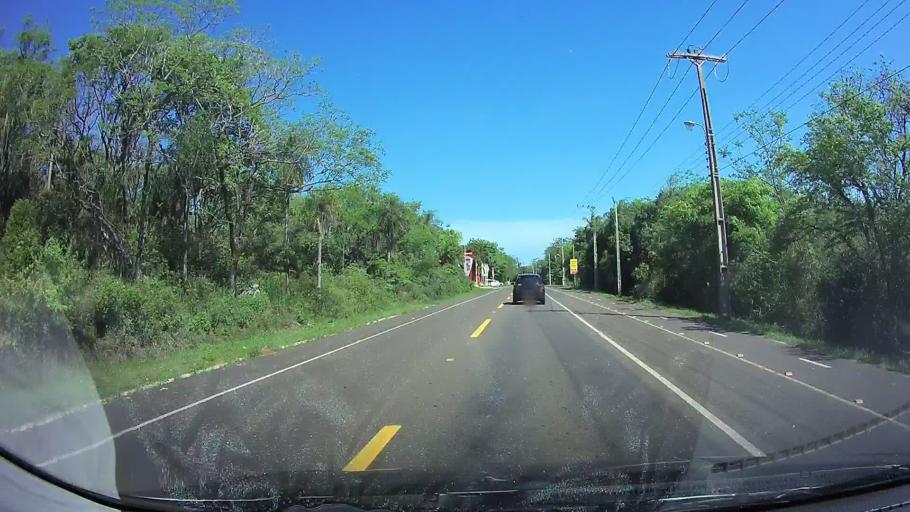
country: PY
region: Cordillera
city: San Bernardino
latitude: -25.2473
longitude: -57.3227
